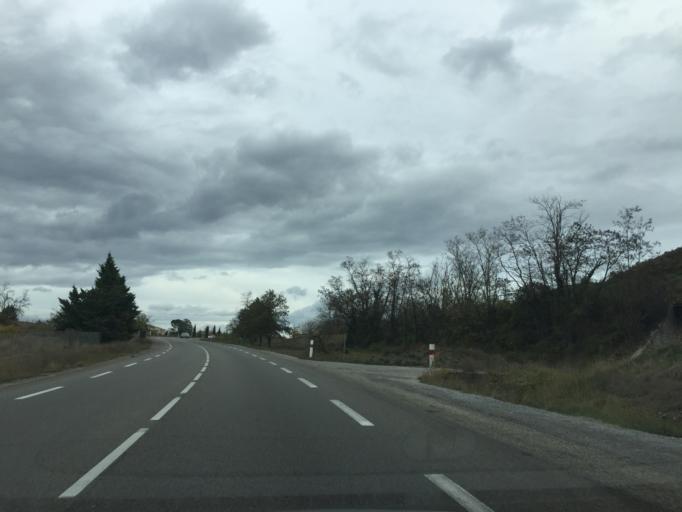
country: FR
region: Rhone-Alpes
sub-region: Departement de l'Ardeche
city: Lachapelle-sous-Aubenas
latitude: 44.5346
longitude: 4.3441
